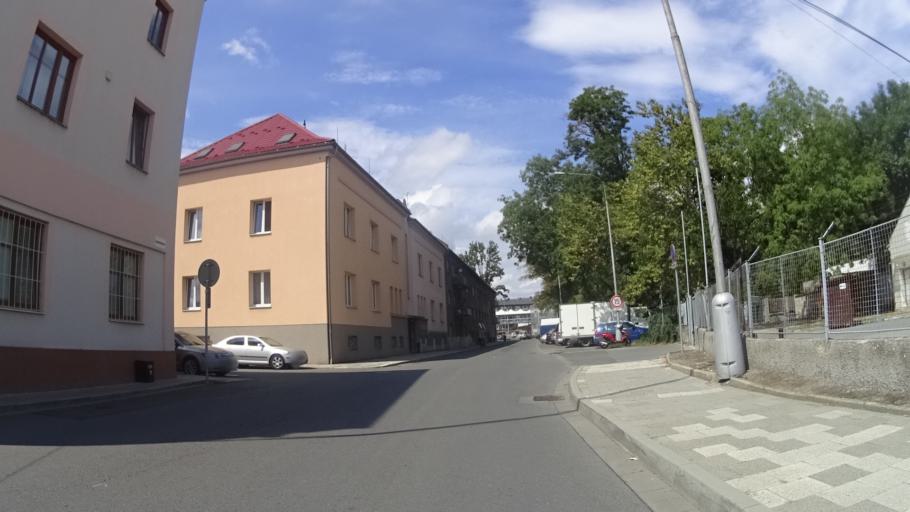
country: CZ
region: Olomoucky
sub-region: Okres Olomouc
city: Olomouc
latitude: 49.5870
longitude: 17.2468
